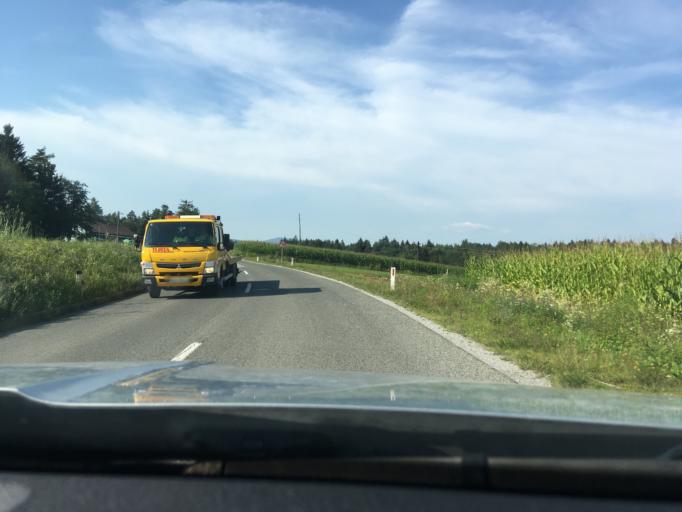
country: SI
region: Crnomelj
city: Crnomelj
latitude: 45.5454
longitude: 15.1613
